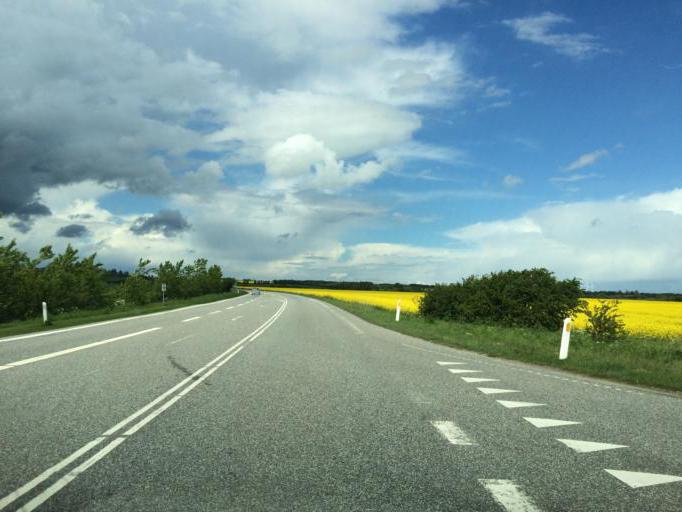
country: DK
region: North Denmark
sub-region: Vesthimmerland Kommune
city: Farso
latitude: 56.6959
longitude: 9.3152
